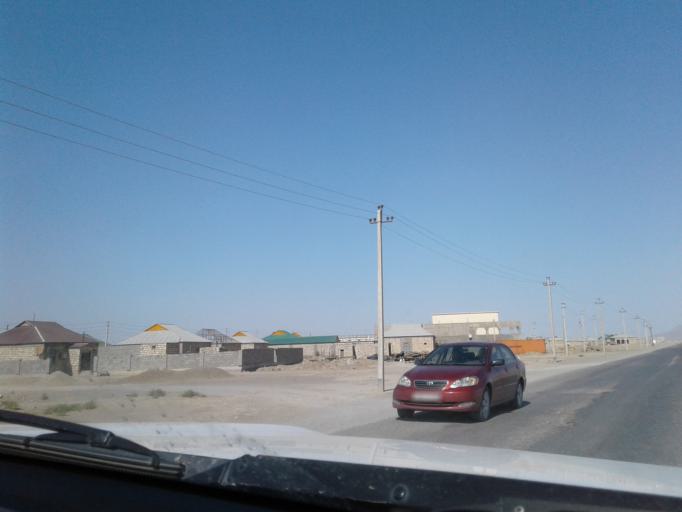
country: TM
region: Balkan
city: Gumdag
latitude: 39.2046
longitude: 54.6183
